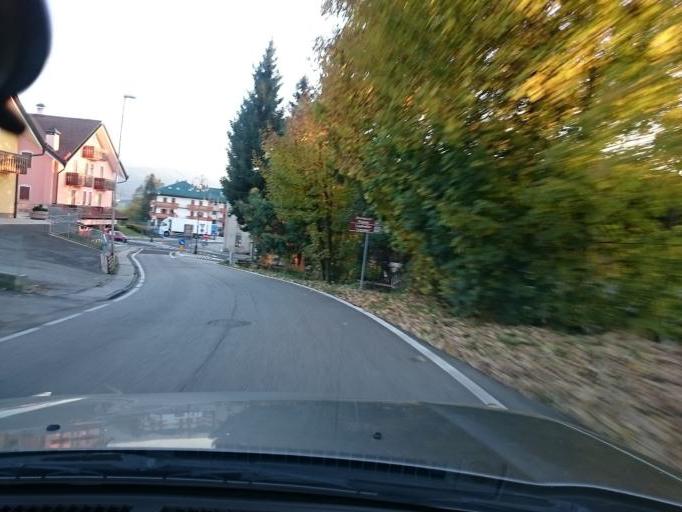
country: IT
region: Veneto
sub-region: Provincia di Vicenza
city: Canove di Roana
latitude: 45.8705
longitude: 11.4794
